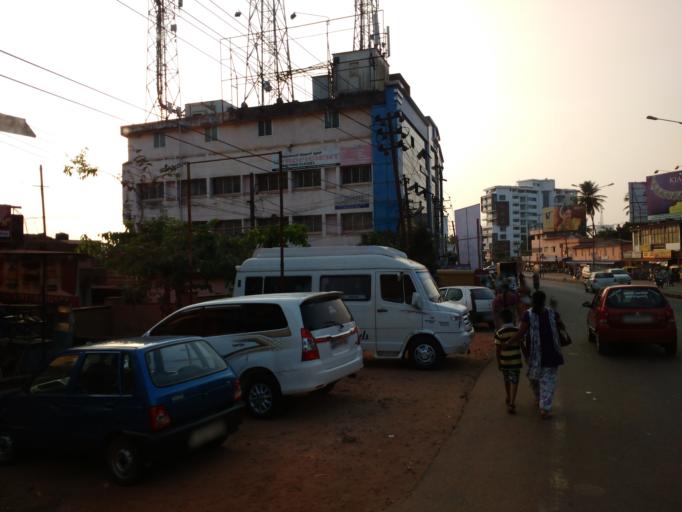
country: IN
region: Karnataka
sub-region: Dakshina Kannada
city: Mangalore
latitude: 12.8845
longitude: 74.8680
